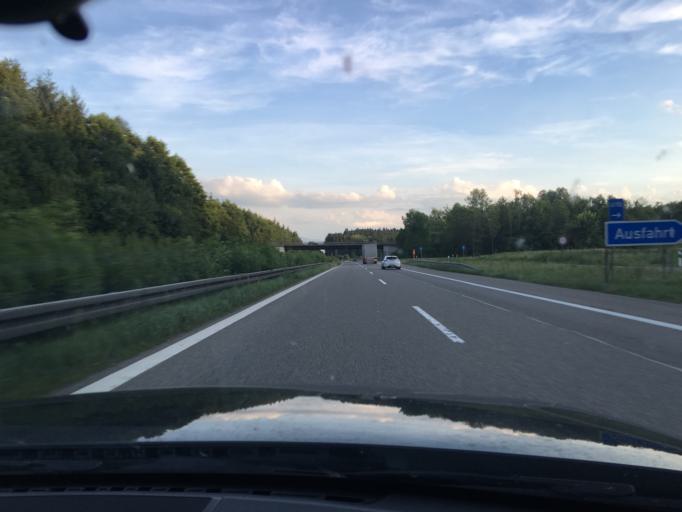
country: DE
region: Bavaria
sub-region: Swabia
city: Weissensberg
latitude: 47.5814
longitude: 9.7356
